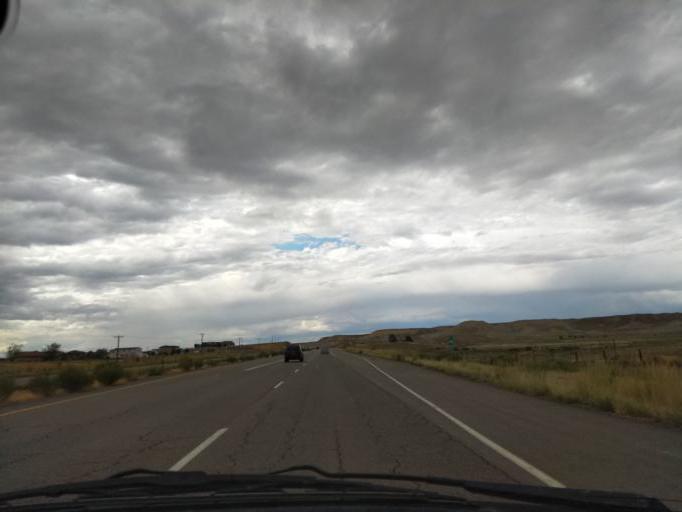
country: US
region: Colorado
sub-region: Mesa County
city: Fruitvale
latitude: 38.9970
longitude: -108.4554
